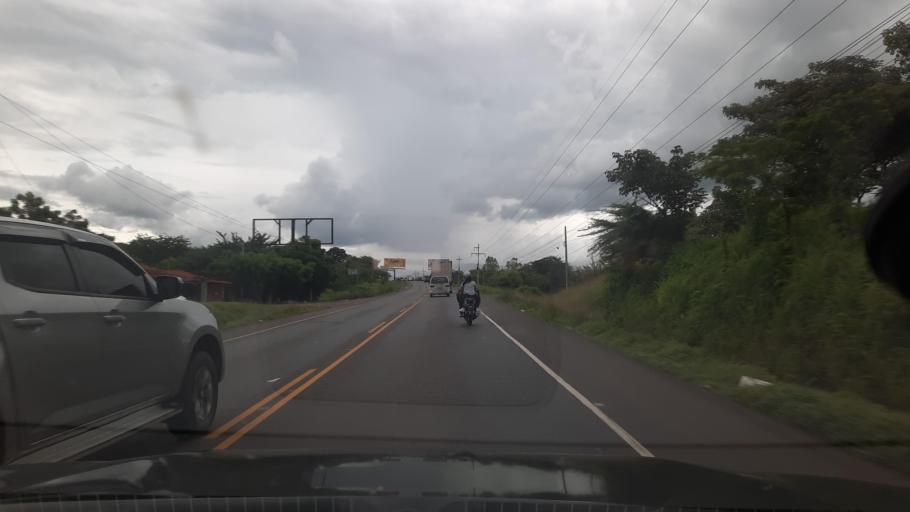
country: HN
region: Choluteca
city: Ciudad Choluteca
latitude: 13.3259
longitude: -87.2199
